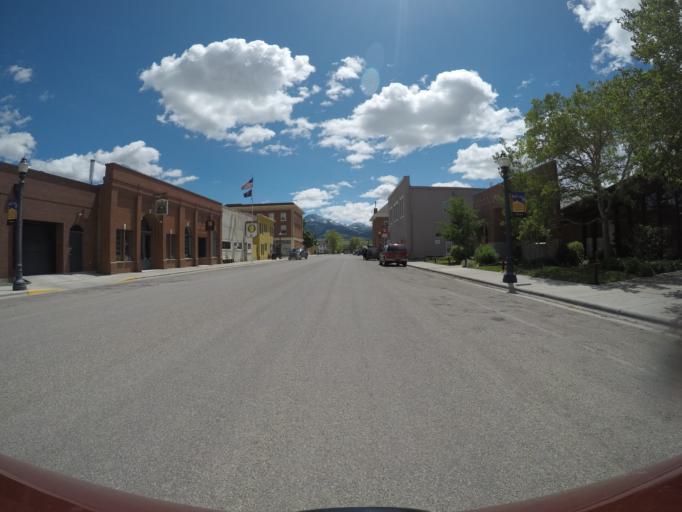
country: US
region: Montana
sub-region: Park County
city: Livingston
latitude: 45.6625
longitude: -110.5593
